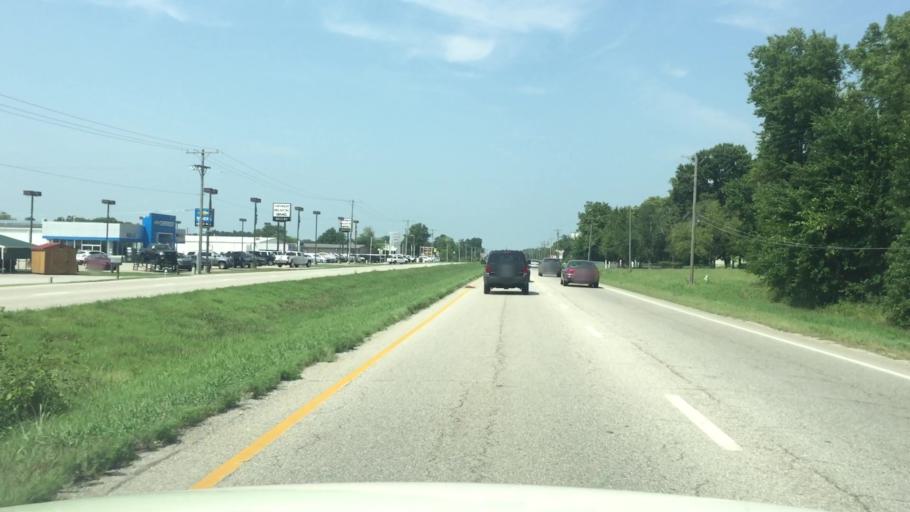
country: US
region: Kansas
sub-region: Crawford County
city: Frontenac
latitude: 37.4572
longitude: -94.7051
